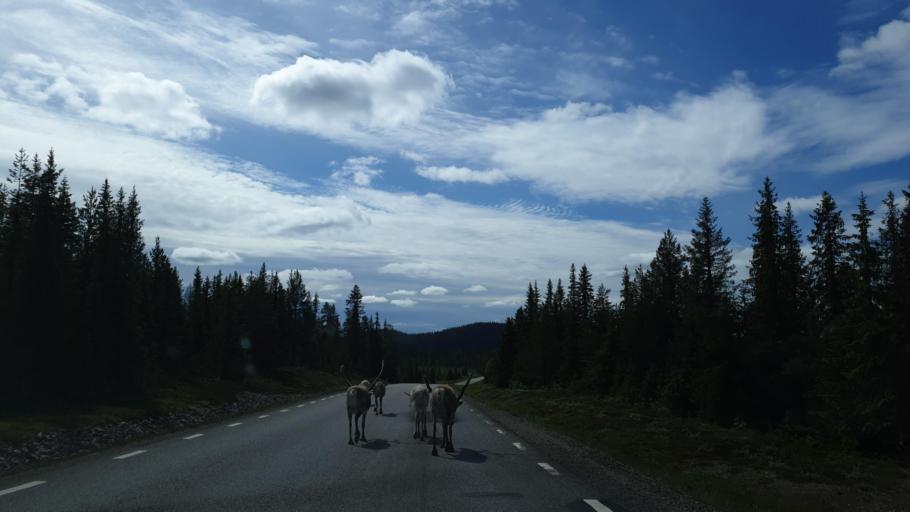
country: SE
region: Vaesterbotten
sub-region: Mala Kommun
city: Mala
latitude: 65.5763
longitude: 18.4338
